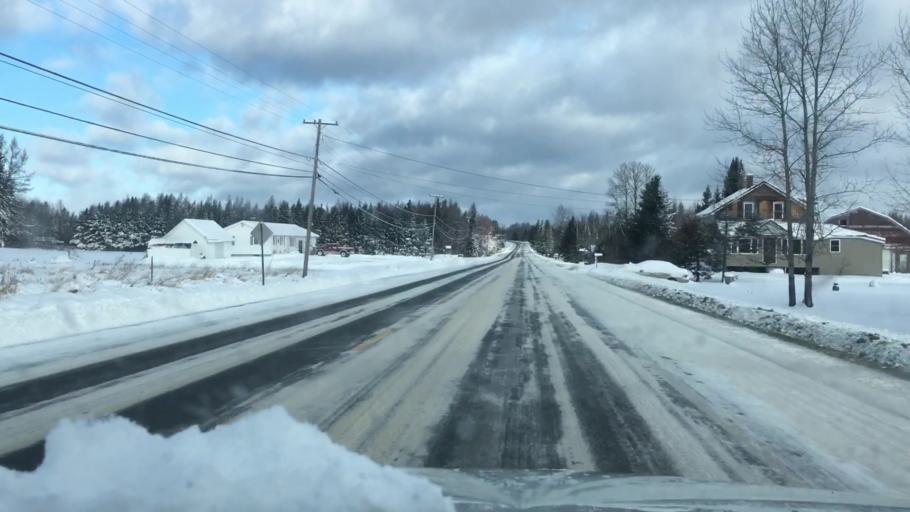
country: US
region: Maine
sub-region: Aroostook County
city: Caribou
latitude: 46.9172
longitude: -68.0188
